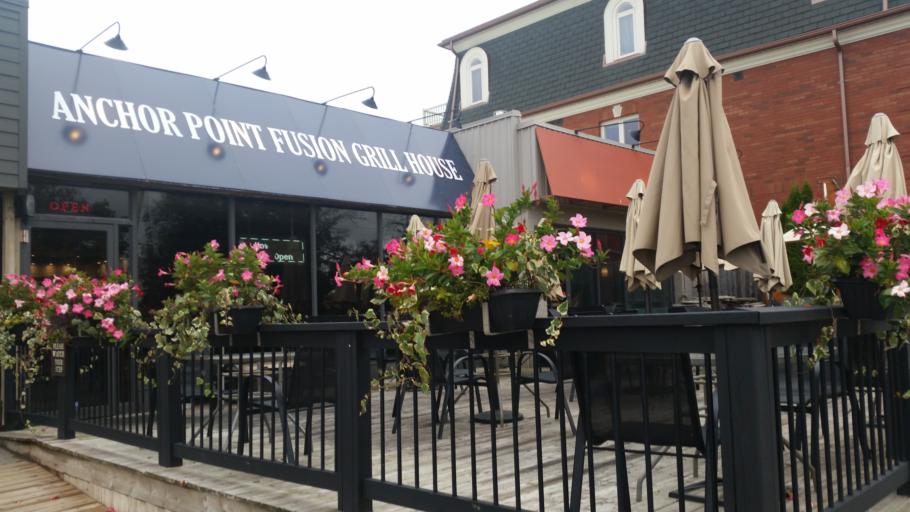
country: CA
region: Ontario
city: Uxbridge
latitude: 44.1046
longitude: -78.9419
